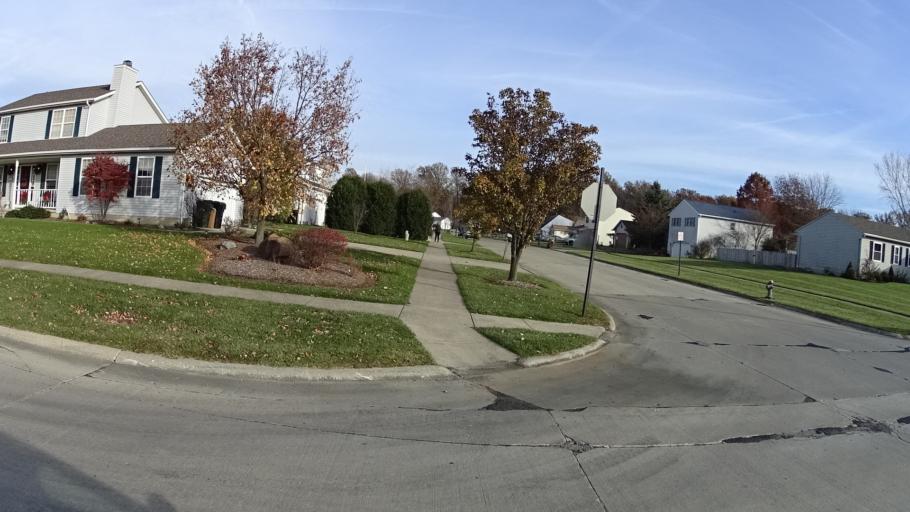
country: US
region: Ohio
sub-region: Lorain County
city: Elyria
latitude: 41.3397
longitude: -82.0755
